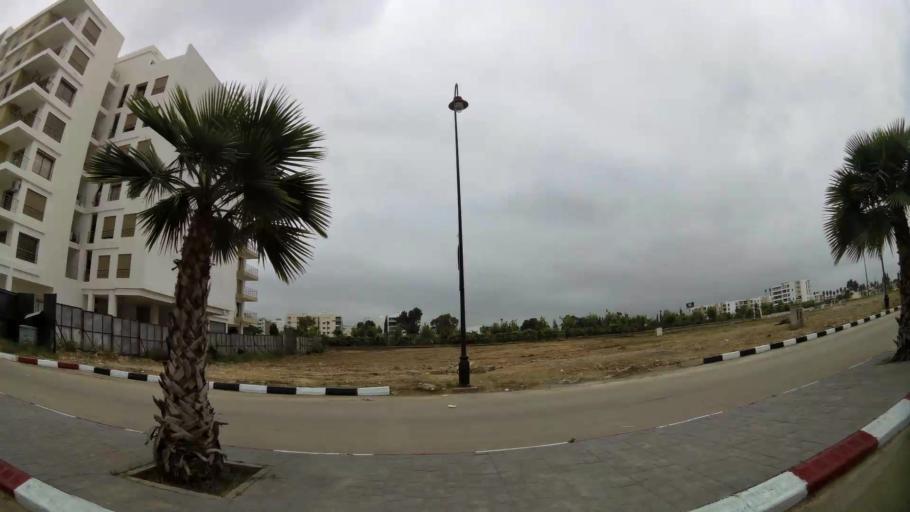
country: MA
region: Fes-Boulemane
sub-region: Fes
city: Fes
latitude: 34.0363
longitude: -5.0130
